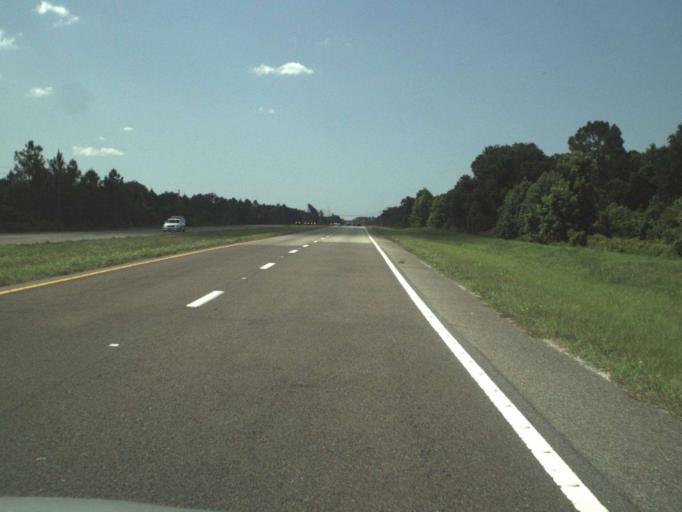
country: US
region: Florida
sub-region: Orange County
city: Christmas
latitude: 28.3974
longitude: -80.9454
